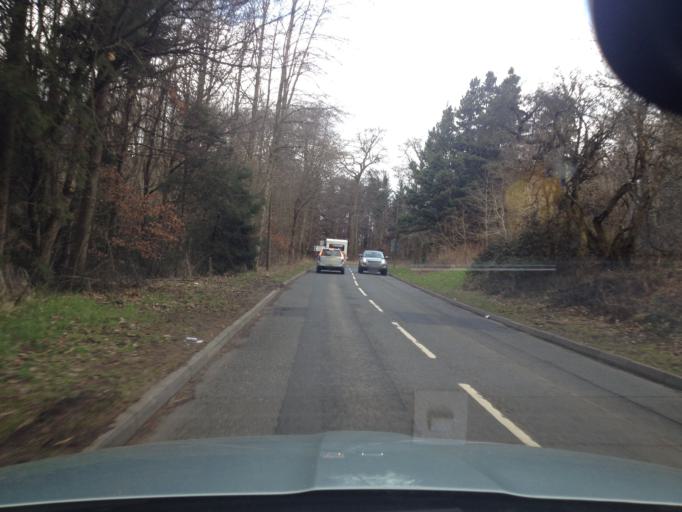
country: GB
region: Scotland
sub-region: West Lothian
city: Mid Calder
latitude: 55.8723
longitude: -3.4983
